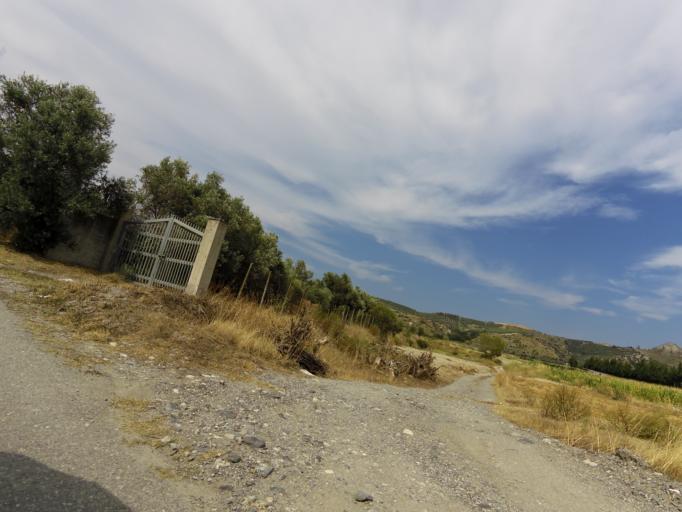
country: IT
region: Calabria
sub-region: Provincia di Reggio Calabria
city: Monasterace
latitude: 38.4548
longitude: 16.5163
